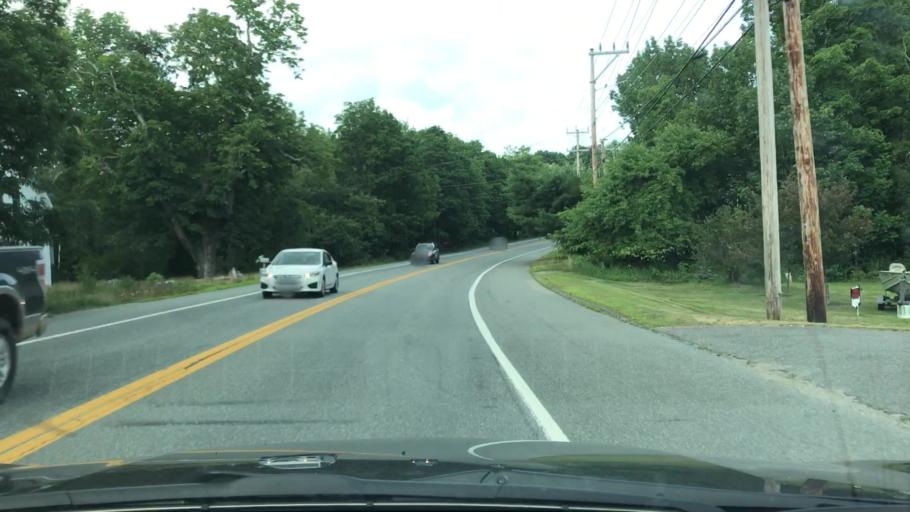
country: US
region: Maine
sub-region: Hancock County
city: Trenton
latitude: 44.4319
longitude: -68.3212
